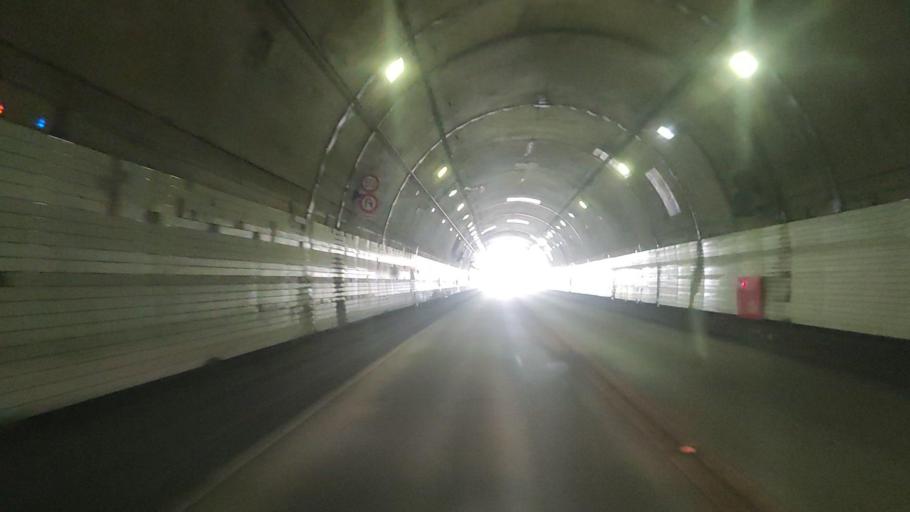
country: JP
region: Fukuoka
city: Maebaru-chuo
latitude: 33.4657
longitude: 130.2782
